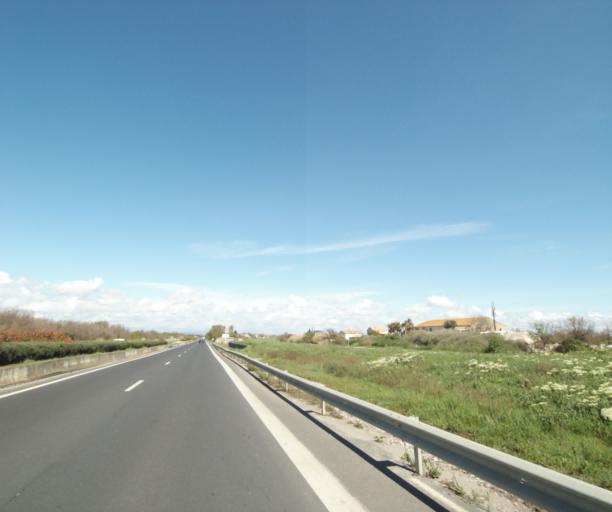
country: FR
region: Languedoc-Roussillon
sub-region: Departement de l'Herault
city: Lattes
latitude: 43.5416
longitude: 3.8972
